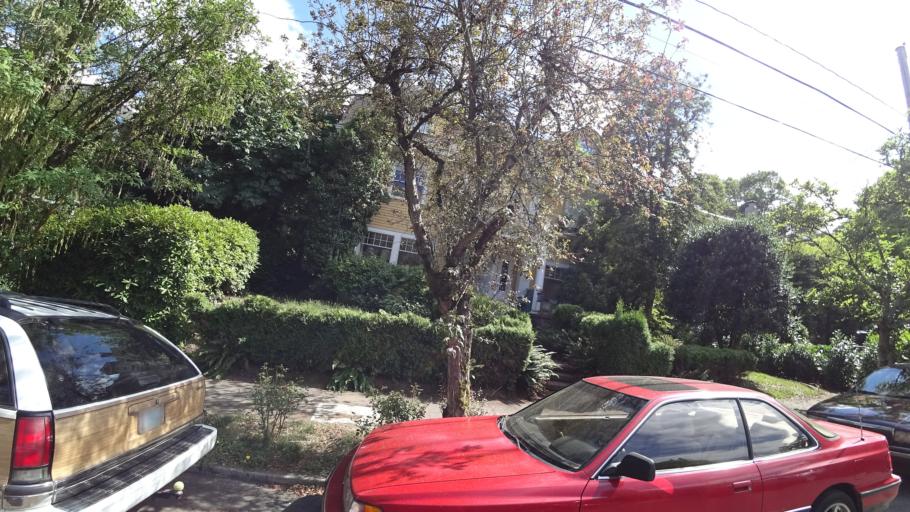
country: US
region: Oregon
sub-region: Multnomah County
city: Portland
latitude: 45.5297
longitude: -122.7043
